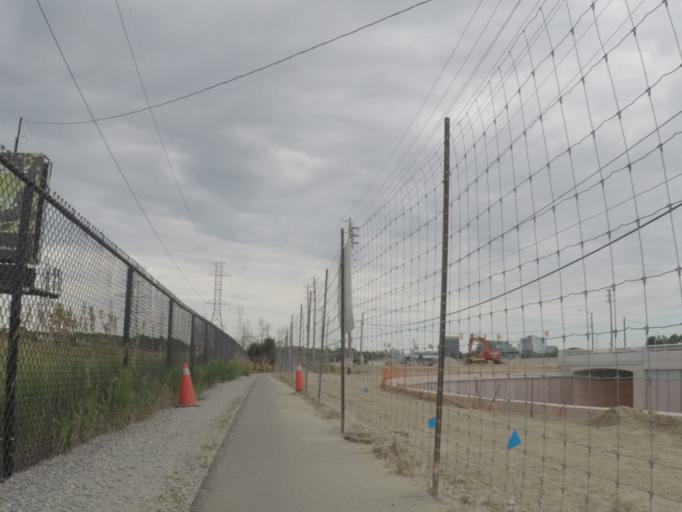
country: CA
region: Ontario
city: Etobicoke
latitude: 43.6673
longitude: -79.5863
